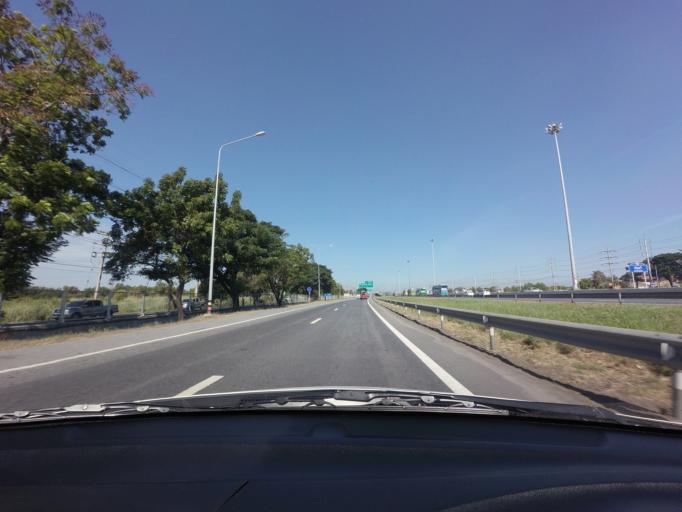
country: TH
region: Pathum Thani
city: Thanyaburi
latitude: 13.9958
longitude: 100.7100
